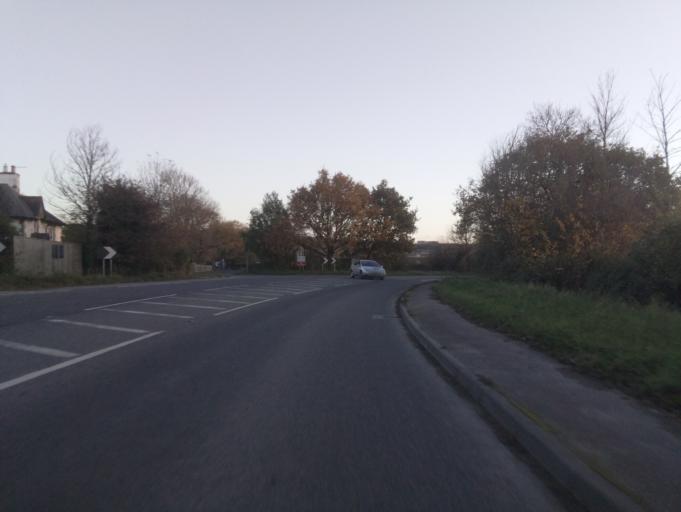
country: GB
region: England
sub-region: Wiltshire
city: Westbury
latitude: 51.2726
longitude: -2.1773
